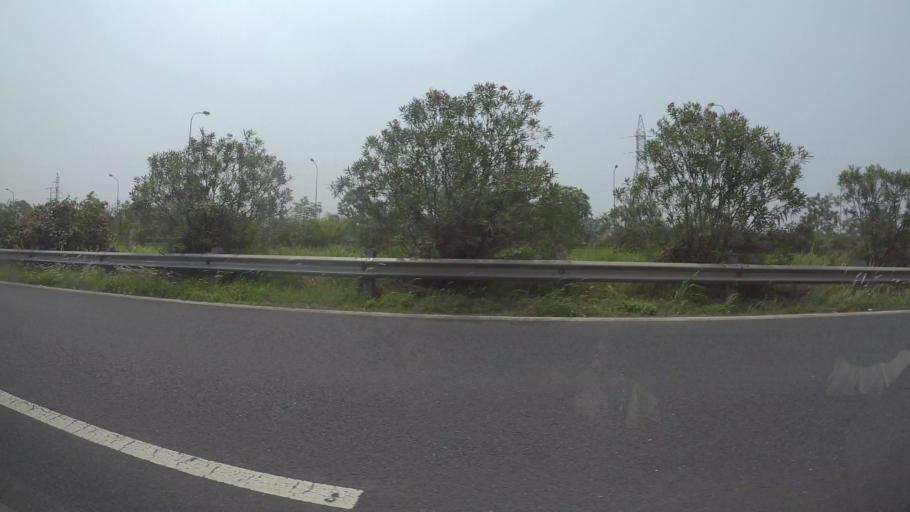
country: VN
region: Ha Noi
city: Quoc Oai
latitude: 21.0025
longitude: 105.6285
